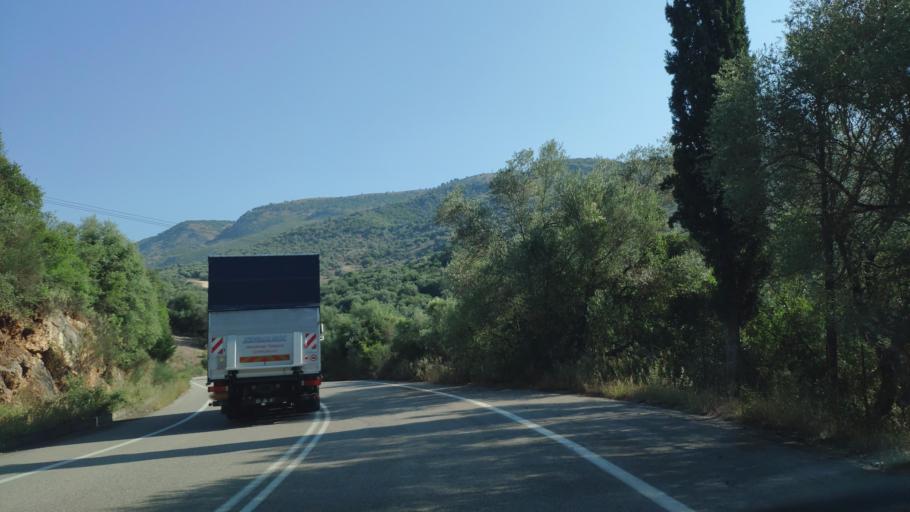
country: GR
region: West Greece
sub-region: Nomos Aitolias kai Akarnanias
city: Stanos
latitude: 38.7749
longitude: 21.1481
